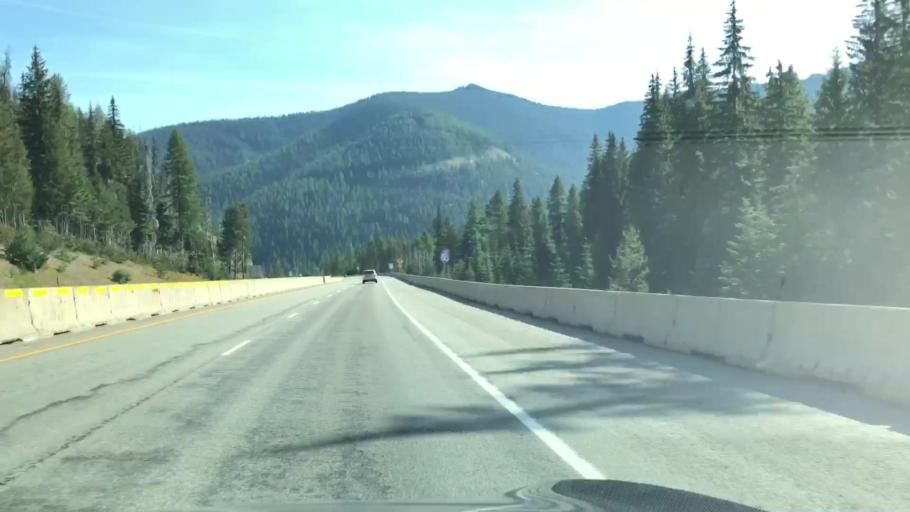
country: US
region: Idaho
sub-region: Shoshone County
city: Wallace
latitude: 47.4507
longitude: -115.6938
